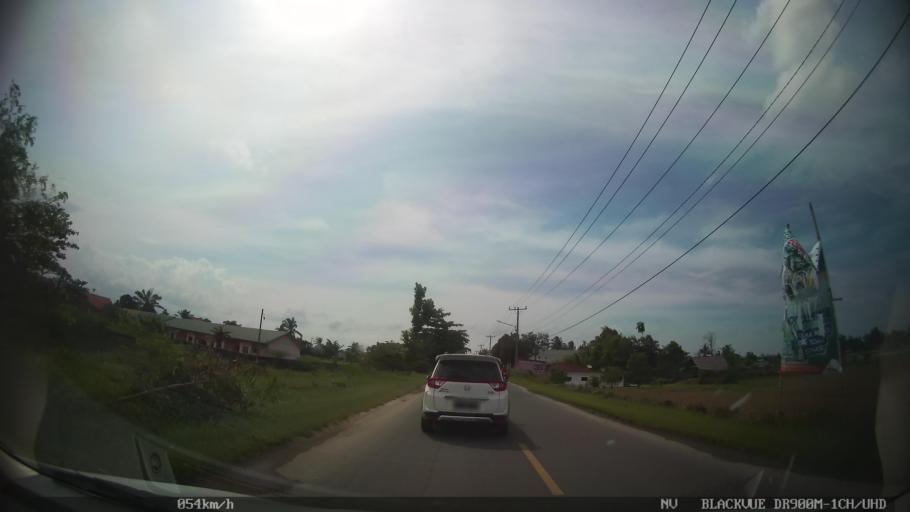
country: ID
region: North Sumatra
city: Percut
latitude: 3.6100
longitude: 98.8490
